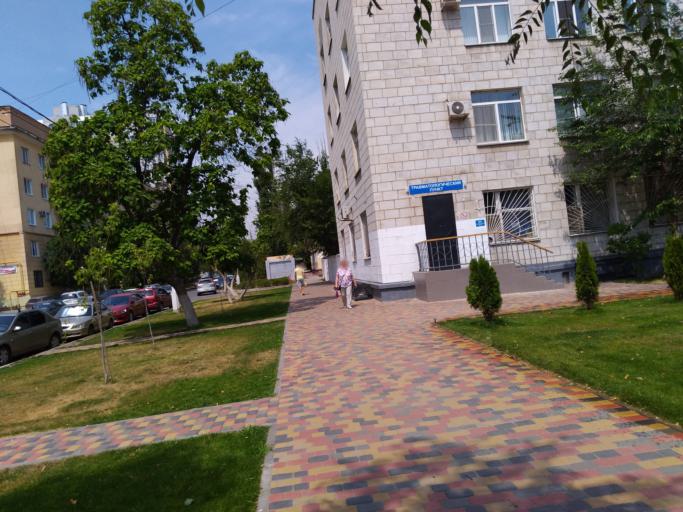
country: RU
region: Volgograd
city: Volgograd
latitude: 48.6965
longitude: 44.4959
